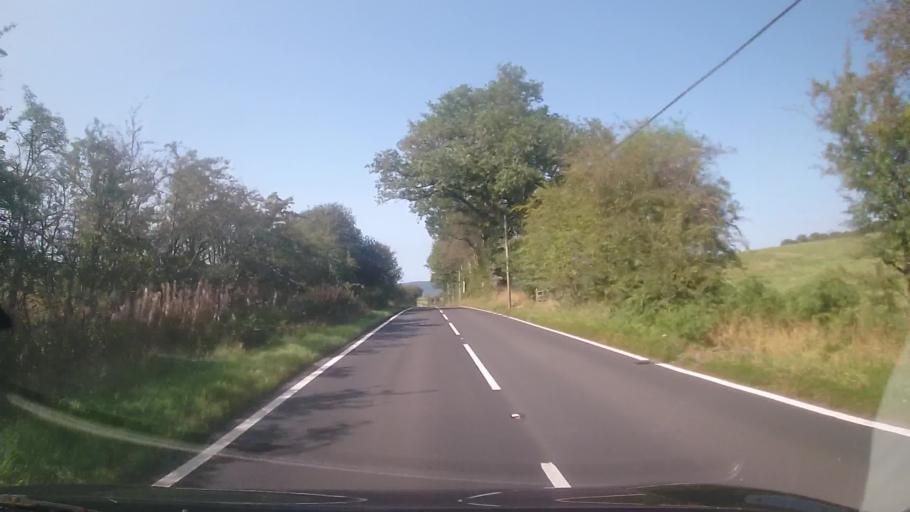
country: GB
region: Wales
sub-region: Sir Powys
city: Builth Wells
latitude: 52.1399
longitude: -3.5528
